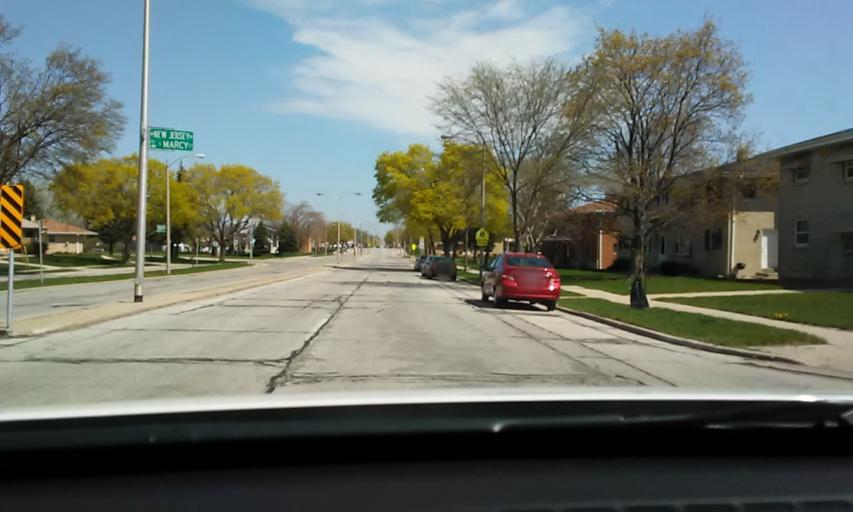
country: US
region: Wisconsin
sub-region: Milwaukee County
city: Greenfield
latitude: 42.9769
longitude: -87.9978
